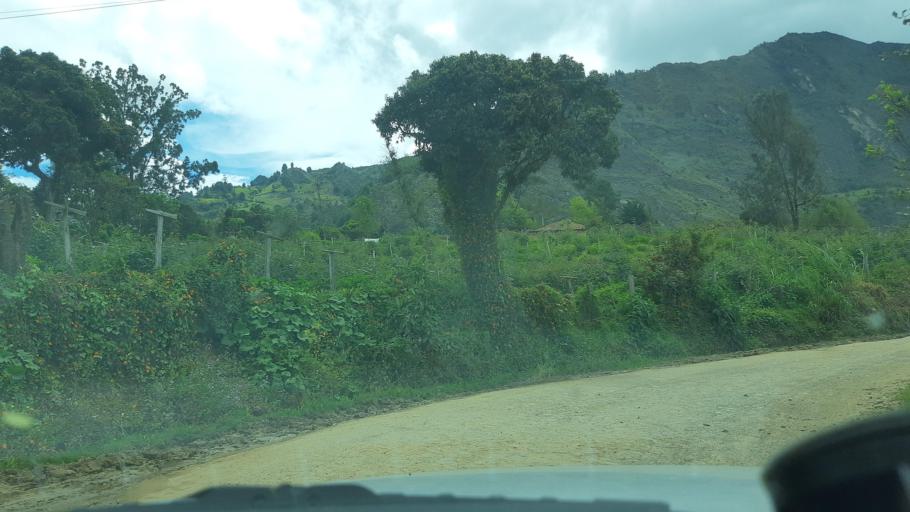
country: CO
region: Cundinamarca
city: Umbita
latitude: 5.2215
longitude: -73.4505
